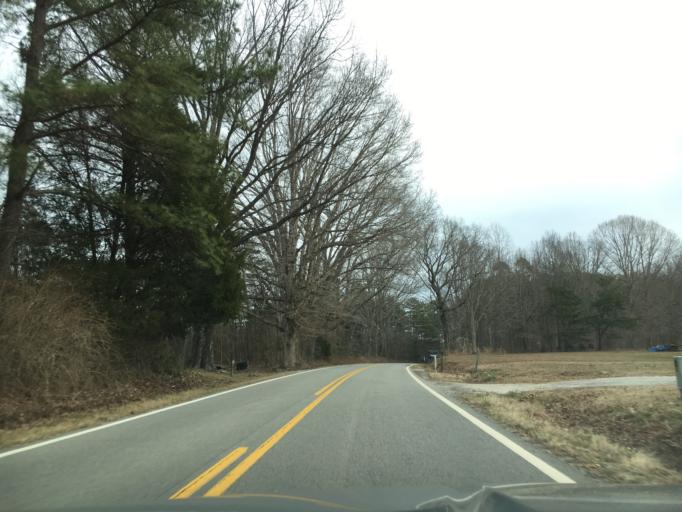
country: US
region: Virginia
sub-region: Charlotte County
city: Charlotte Court House
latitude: 37.1470
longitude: -78.7534
